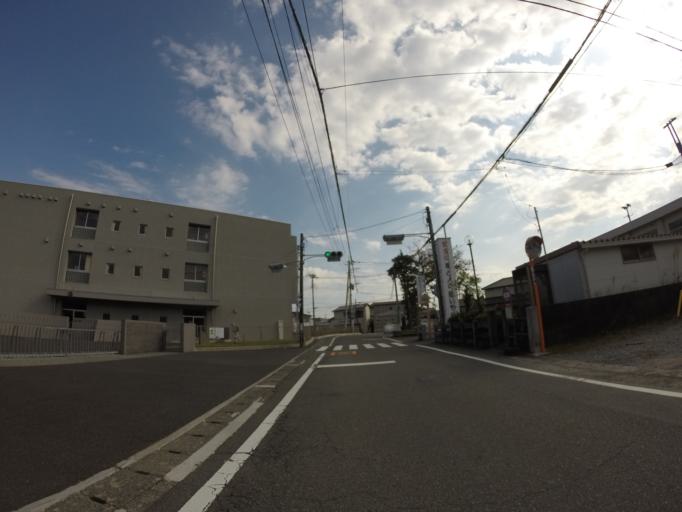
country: JP
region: Shizuoka
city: Fuji
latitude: 35.1644
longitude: 138.6321
